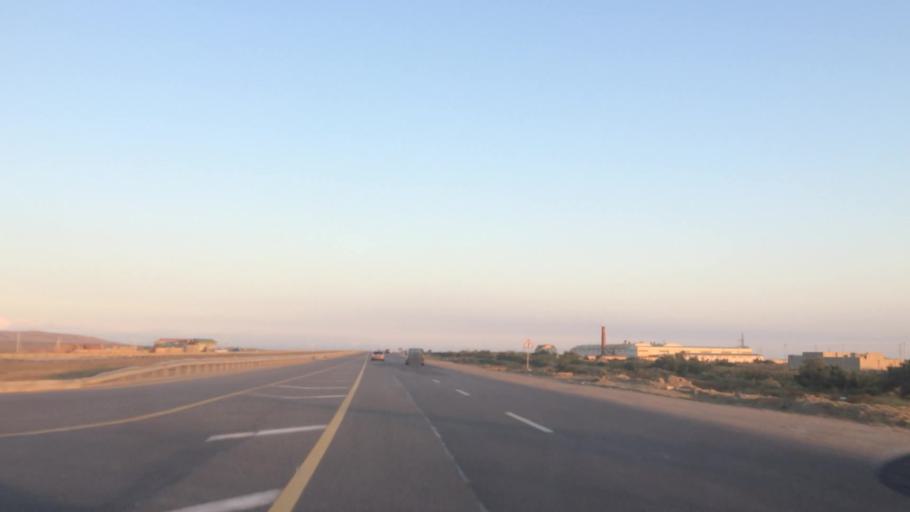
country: AZ
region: Baki
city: Qobustan
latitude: 39.9671
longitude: 49.2733
